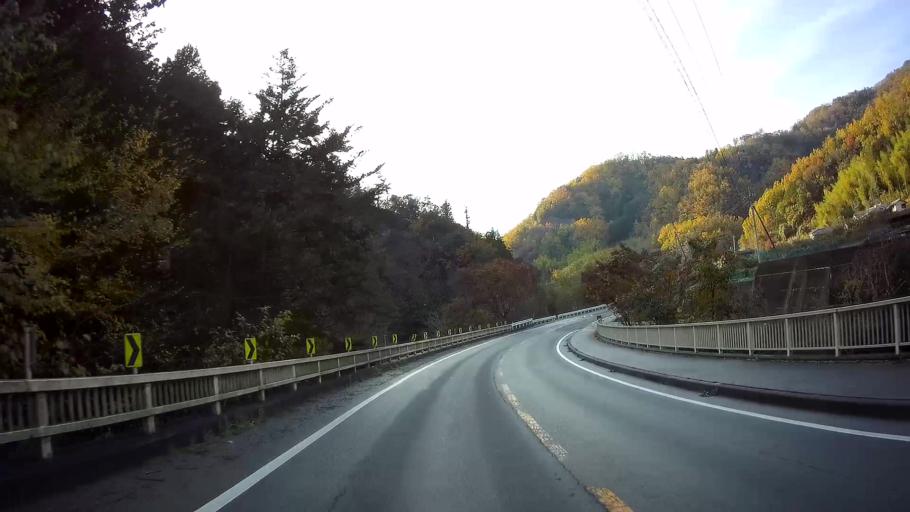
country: JP
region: Yamanashi
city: Ryuo
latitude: 35.4657
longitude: 138.5049
